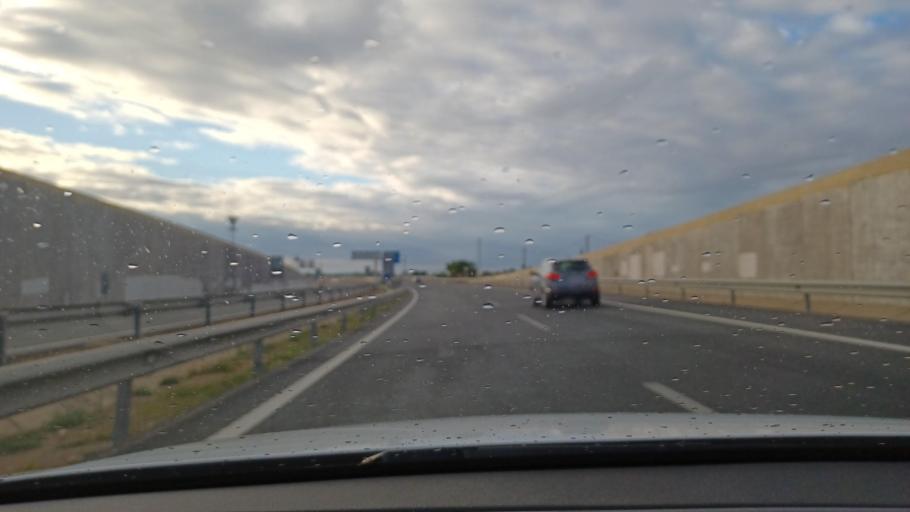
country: ES
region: Valencia
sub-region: Provincia de Alicante
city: Elche
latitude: 38.2958
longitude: -0.6690
